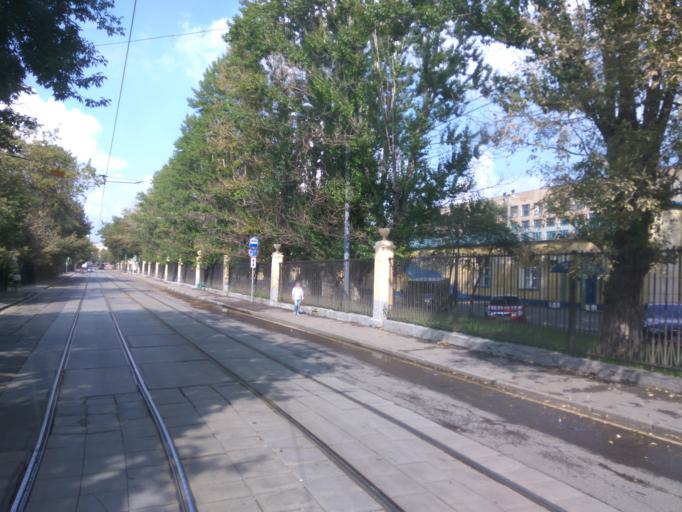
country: RU
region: Moscow
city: Taganskiy
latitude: 55.7601
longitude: 37.6730
